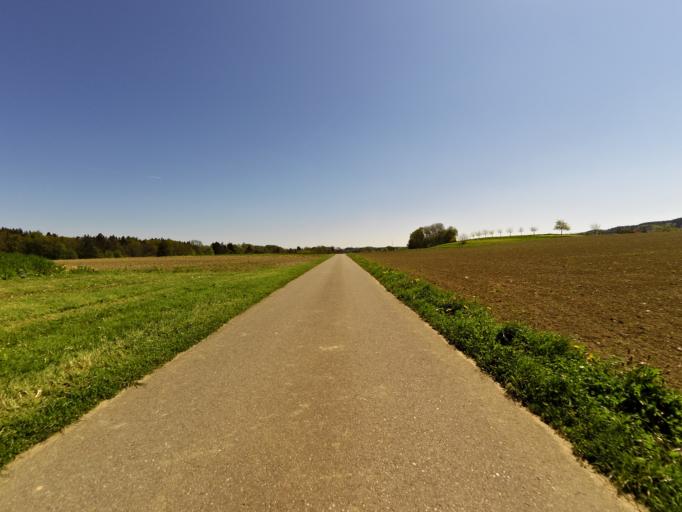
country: CH
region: Thurgau
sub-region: Weinfelden District
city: Weinfelden
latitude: 47.6023
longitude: 9.1186
